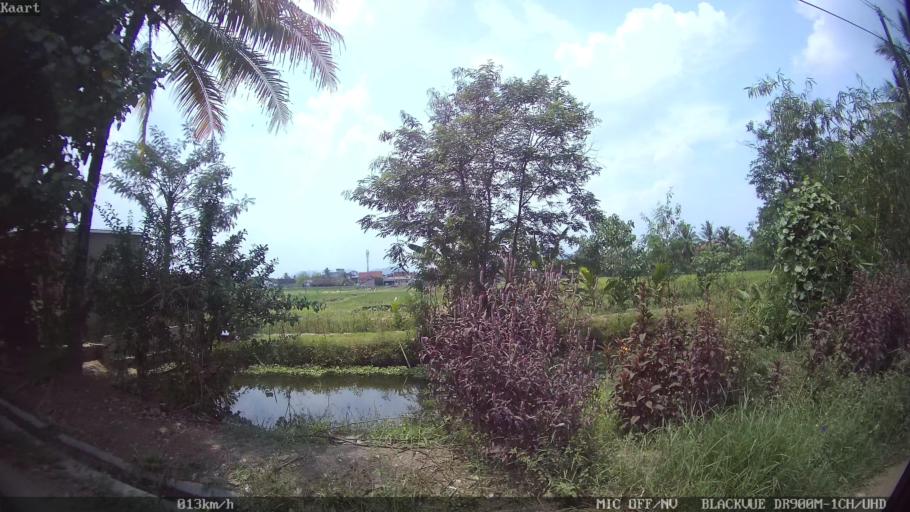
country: ID
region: Lampung
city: Pringsewu
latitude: -5.3579
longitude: 104.9960
